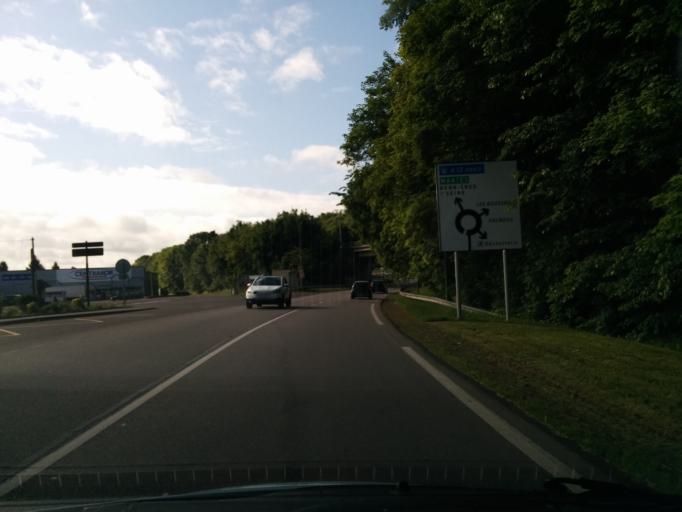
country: FR
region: Haute-Normandie
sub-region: Departement de l'Eure
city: Vernon
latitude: 49.0815
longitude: 1.5043
